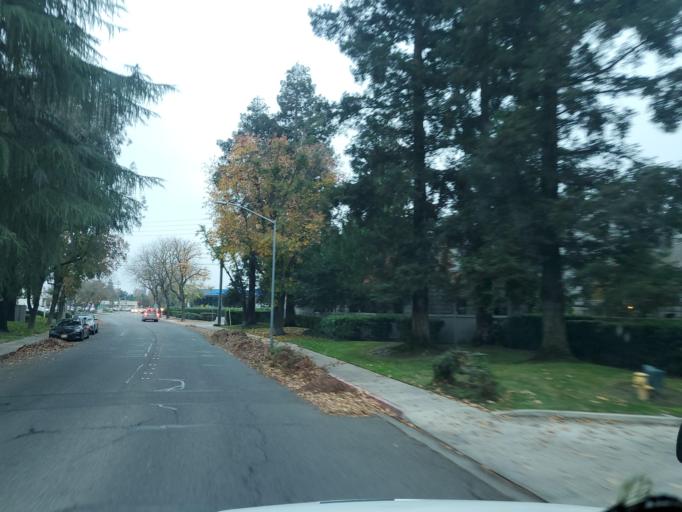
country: US
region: California
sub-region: Stanislaus County
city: Modesto
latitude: 37.6816
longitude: -120.9967
